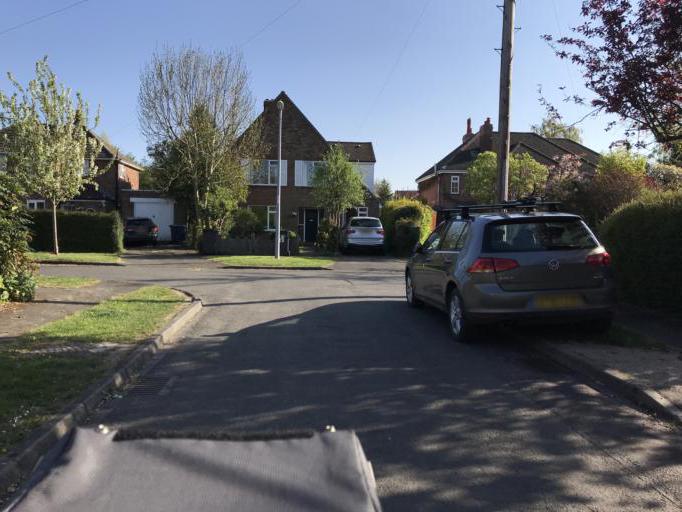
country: GB
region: England
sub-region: Cambridgeshire
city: Cambridge
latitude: 52.1793
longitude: 0.1588
